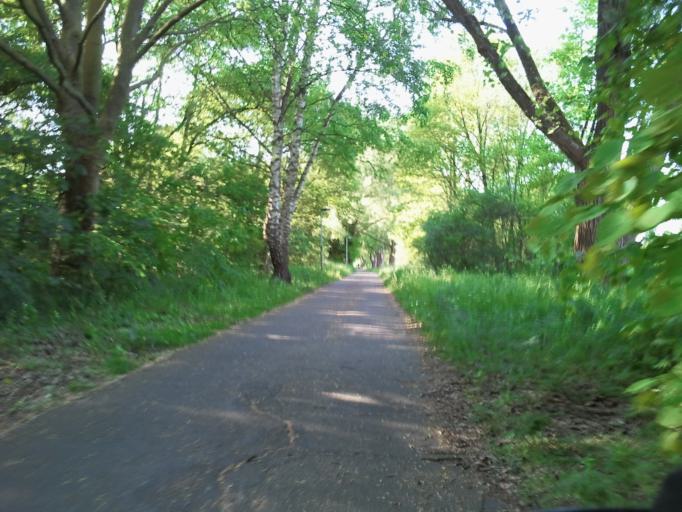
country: DE
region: Lower Saxony
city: Nienburg
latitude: 52.6362
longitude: 9.2311
